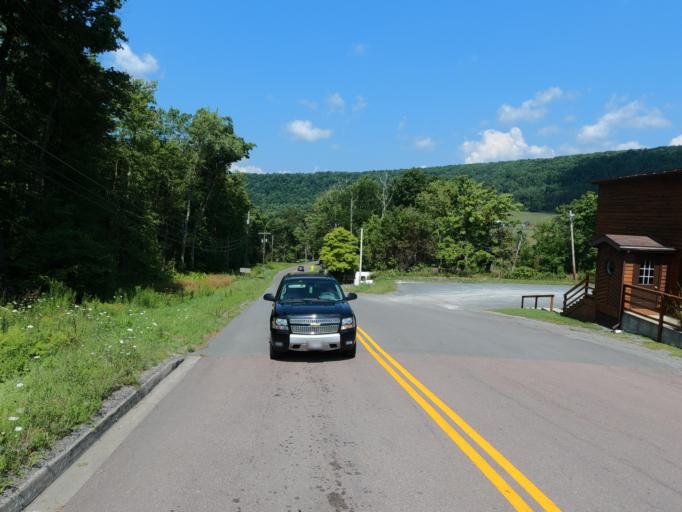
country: US
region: Maryland
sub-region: Garrett County
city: Mountain Lake Park
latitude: 39.4930
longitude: -79.3430
